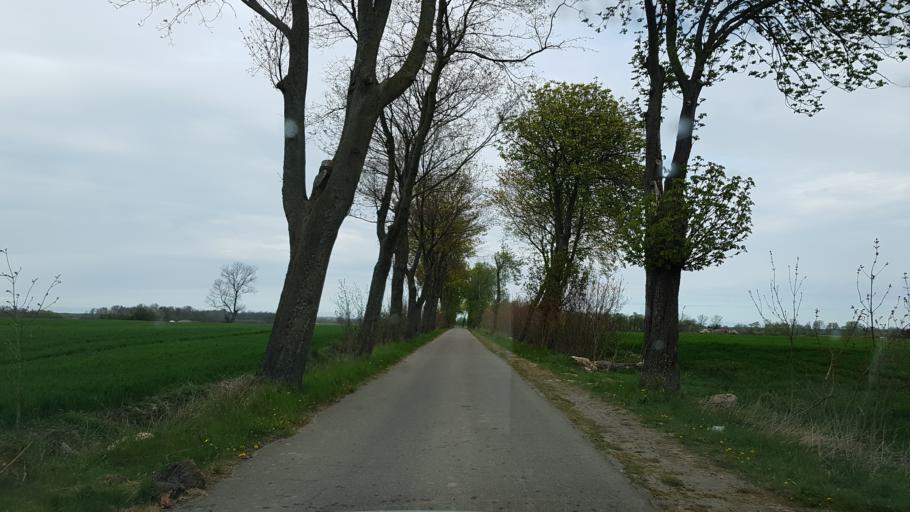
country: PL
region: West Pomeranian Voivodeship
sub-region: Powiat slawienski
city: Slawno
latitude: 54.5094
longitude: 16.5984
